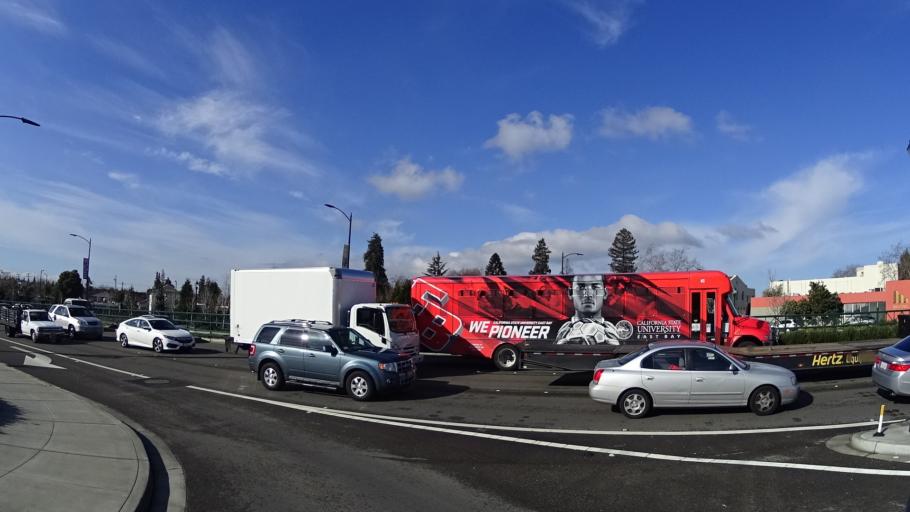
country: US
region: California
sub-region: Alameda County
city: Hayward
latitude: 37.6702
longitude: -122.0804
